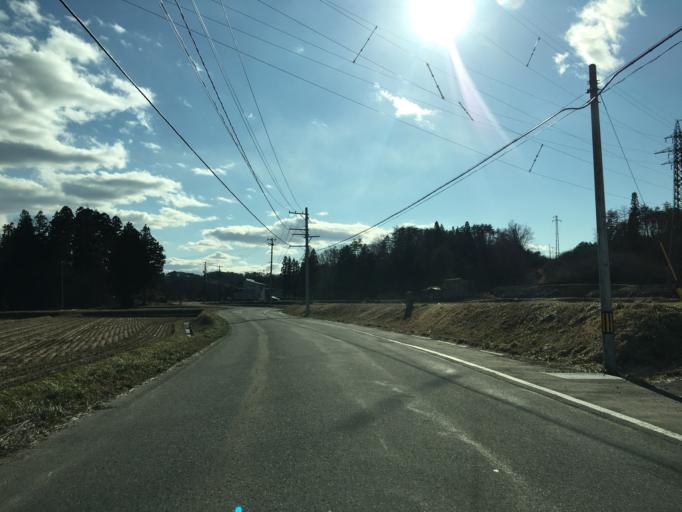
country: JP
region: Yamagata
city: Nagai
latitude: 37.9971
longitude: 140.0112
